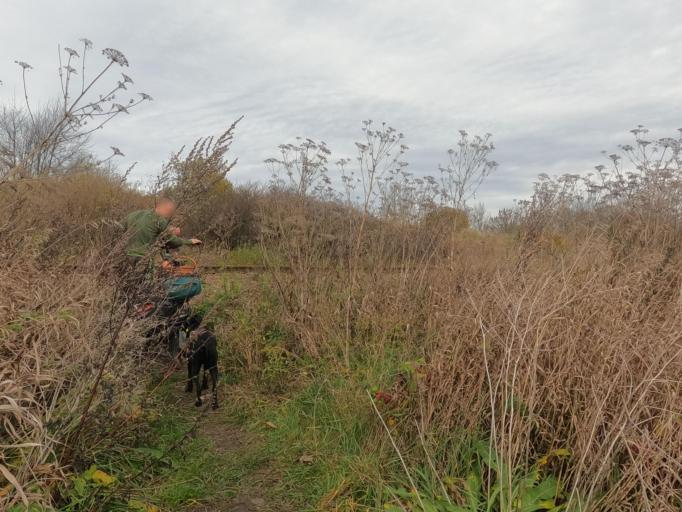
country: PL
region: Pomeranian Voivodeship
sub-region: Powiat starogardzki
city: Starogard Gdanski
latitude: 53.9726
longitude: 18.5128
